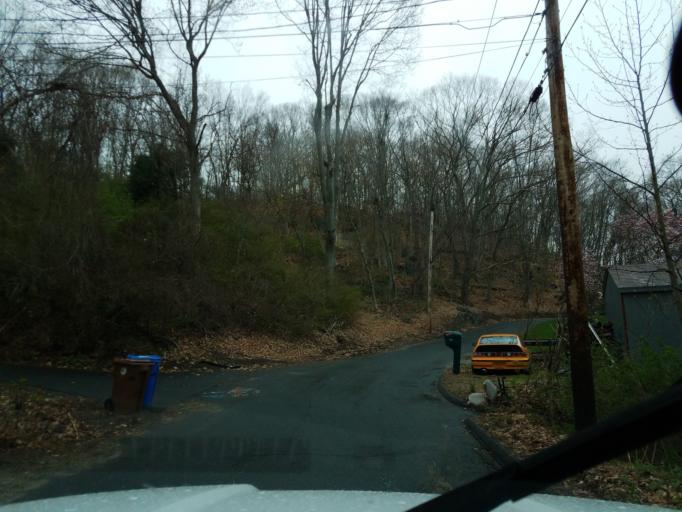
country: US
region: Connecticut
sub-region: Fairfield County
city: Shelton
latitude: 41.3046
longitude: -73.0815
